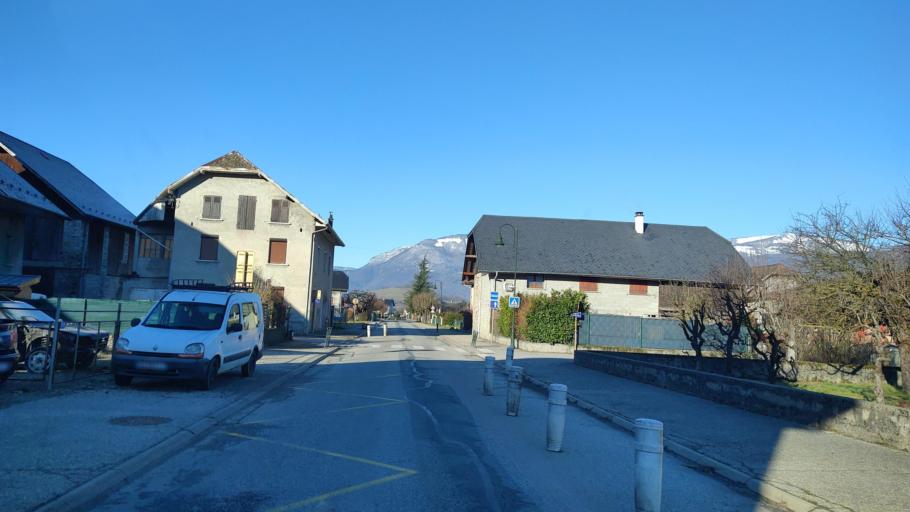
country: FR
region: Rhone-Alpes
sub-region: Departement de la Savoie
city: Aiton
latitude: 45.5519
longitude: 6.2211
